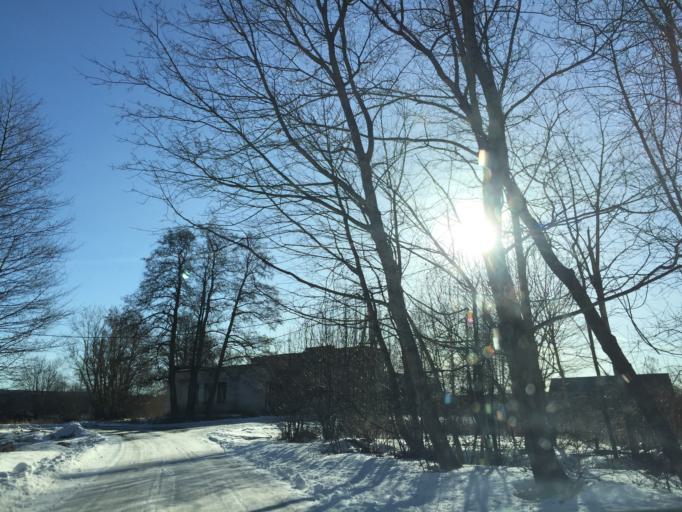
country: LV
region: Salacgrivas
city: Ainazi
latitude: 58.0848
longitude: 24.4949
